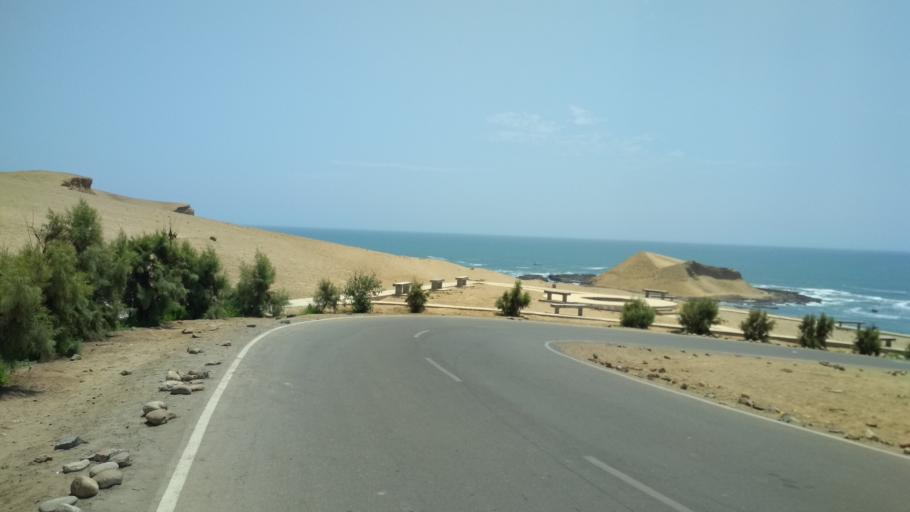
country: PE
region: Lima
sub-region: Barranca
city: Puerto Supe
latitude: -10.8090
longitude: -77.7477
